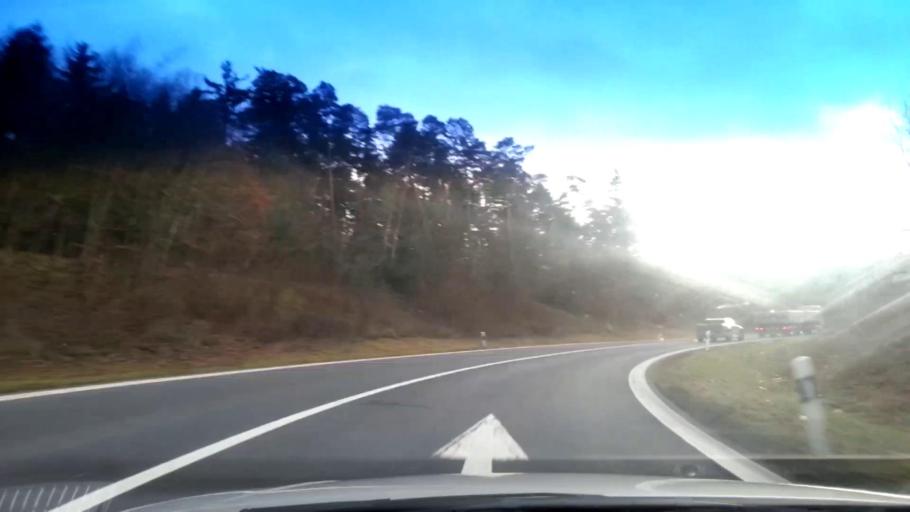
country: DE
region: Bavaria
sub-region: Upper Franconia
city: Zapfendorf
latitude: 50.0126
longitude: 10.9453
